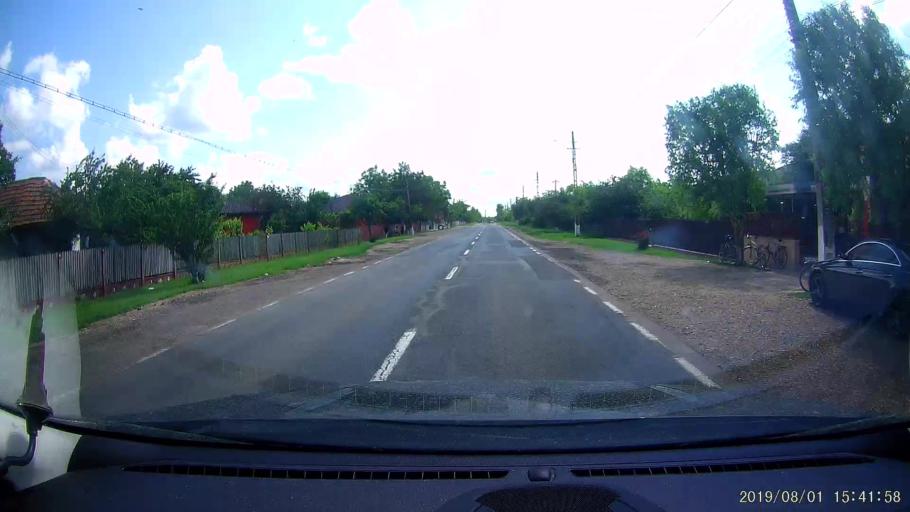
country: RO
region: Braila
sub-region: Comuna Baraganul
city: Baraganul
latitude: 44.8168
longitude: 27.5196
